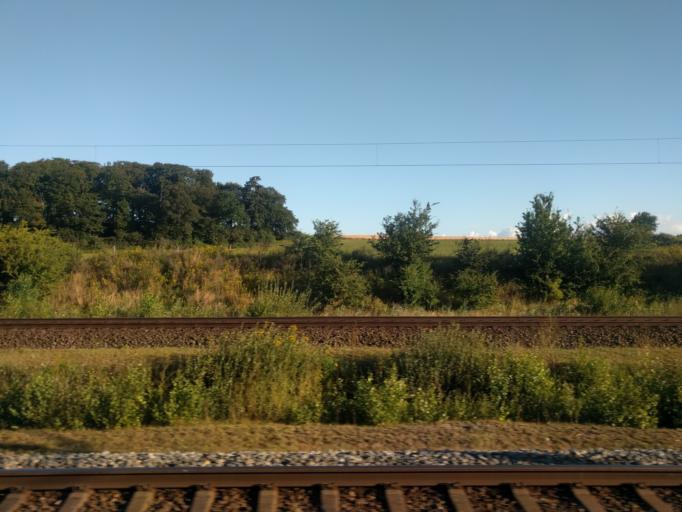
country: DK
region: Zealand
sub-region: Slagelse Kommune
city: Korsor
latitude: 55.3561
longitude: 11.1286
